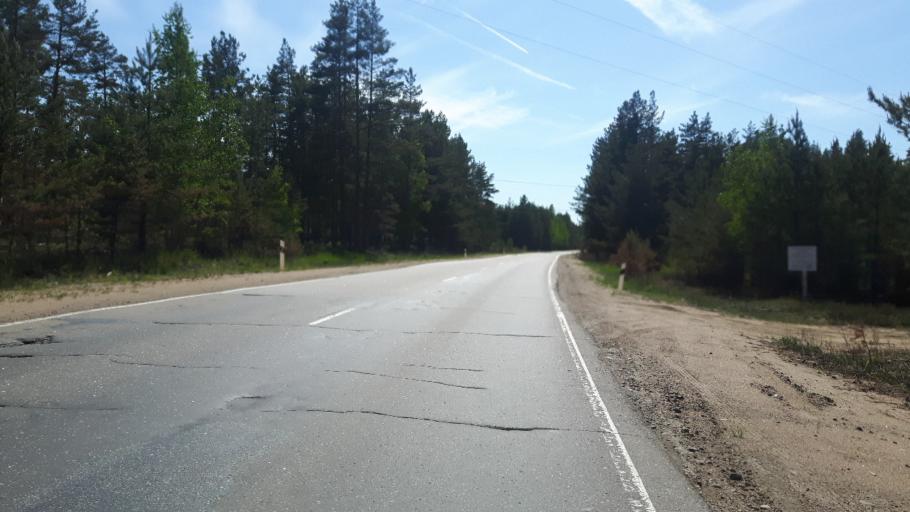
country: RU
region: Leningrad
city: Sista-Palkino
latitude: 59.7805
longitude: 28.8710
